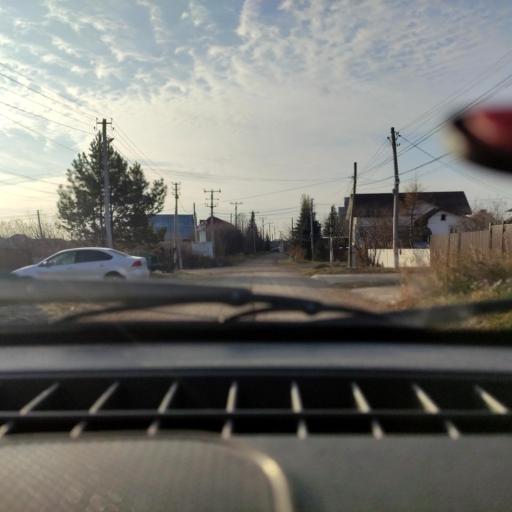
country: RU
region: Bashkortostan
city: Ufa
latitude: 54.6091
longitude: 55.9306
